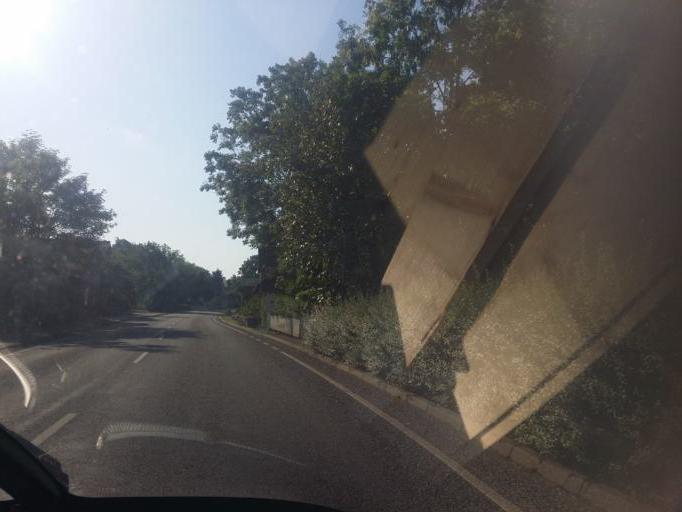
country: DE
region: Schleswig-Holstein
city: Neukirchen
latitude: 54.9020
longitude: 8.7518
